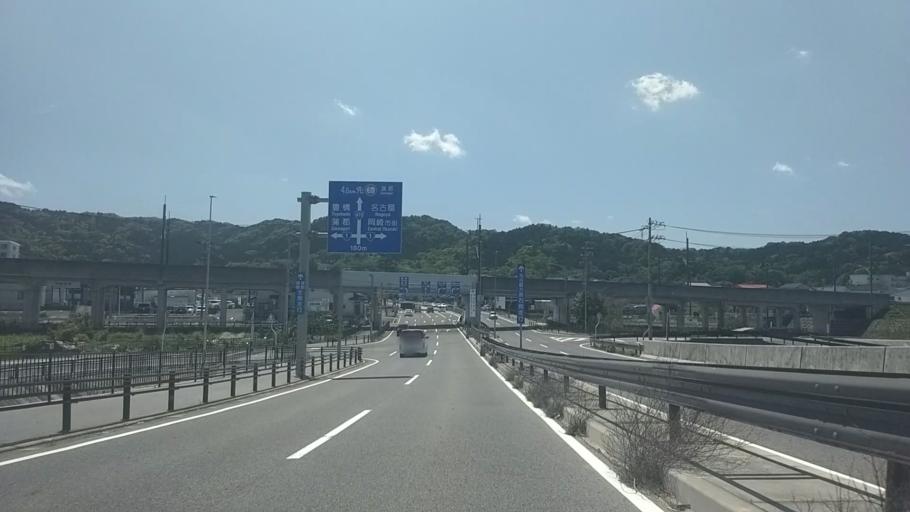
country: JP
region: Aichi
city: Gamagori
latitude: 34.8967
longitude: 137.2555
